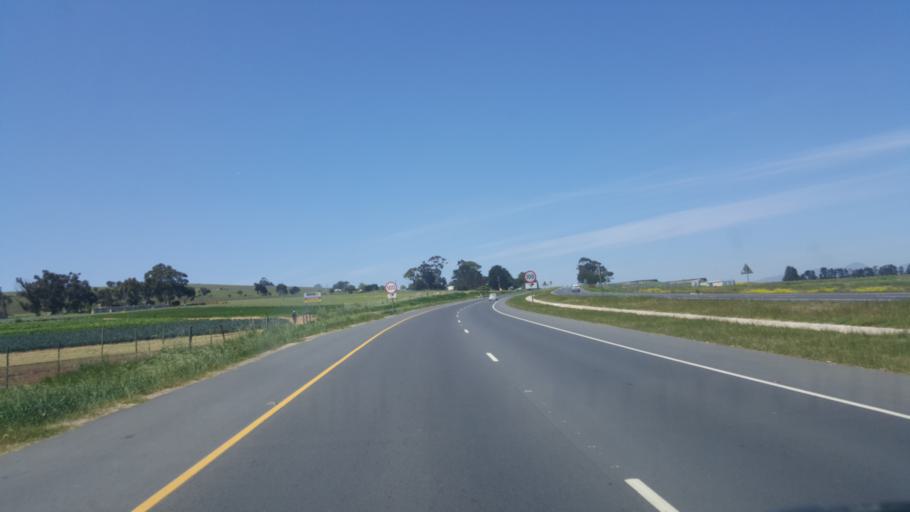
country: ZA
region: Western Cape
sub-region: City of Cape Town
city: Kraaifontein
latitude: -33.9527
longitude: 18.7167
